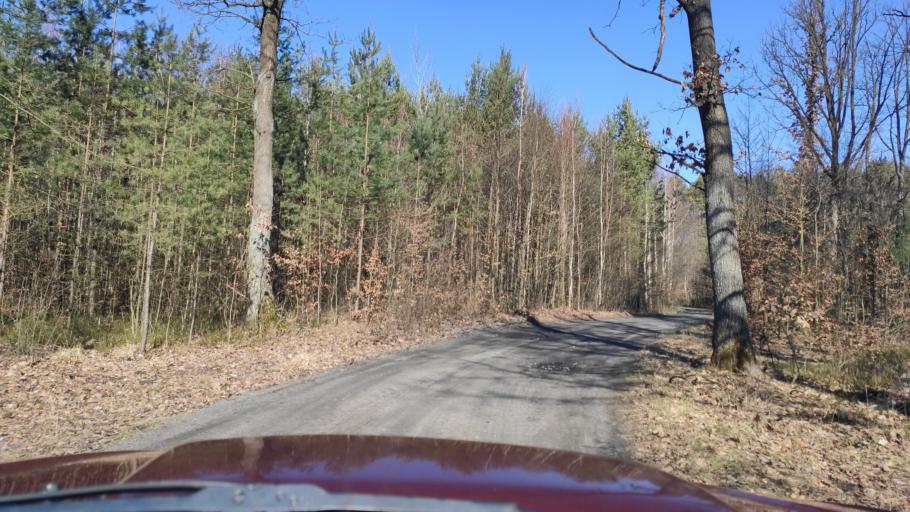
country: PL
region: Masovian Voivodeship
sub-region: Powiat kozienicki
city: Garbatka-Letnisko
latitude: 51.4421
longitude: 21.5361
